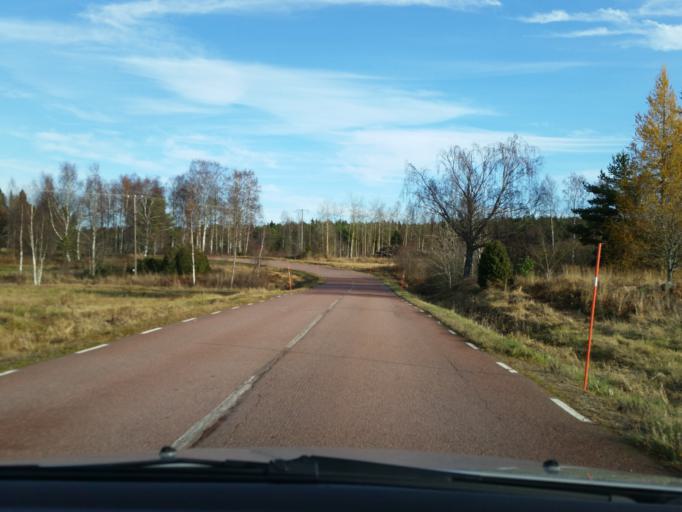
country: AX
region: Alands landsbygd
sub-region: Saltvik
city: Saltvik
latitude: 60.3168
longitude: 20.0698
